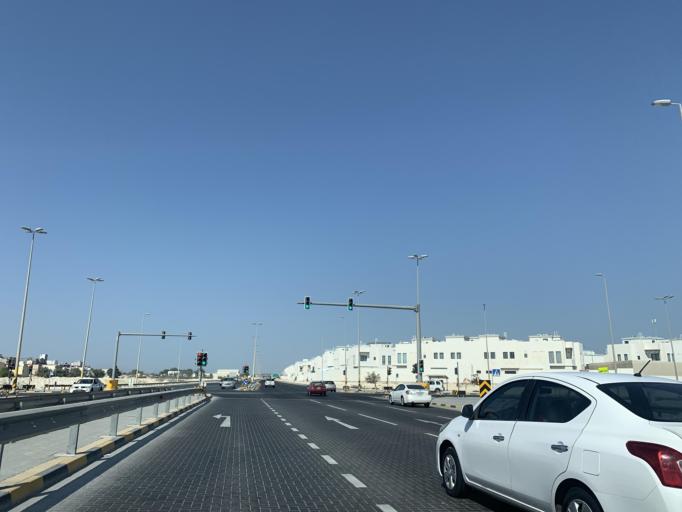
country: BH
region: Central Governorate
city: Madinat Hamad
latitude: 26.1259
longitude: 50.4844
